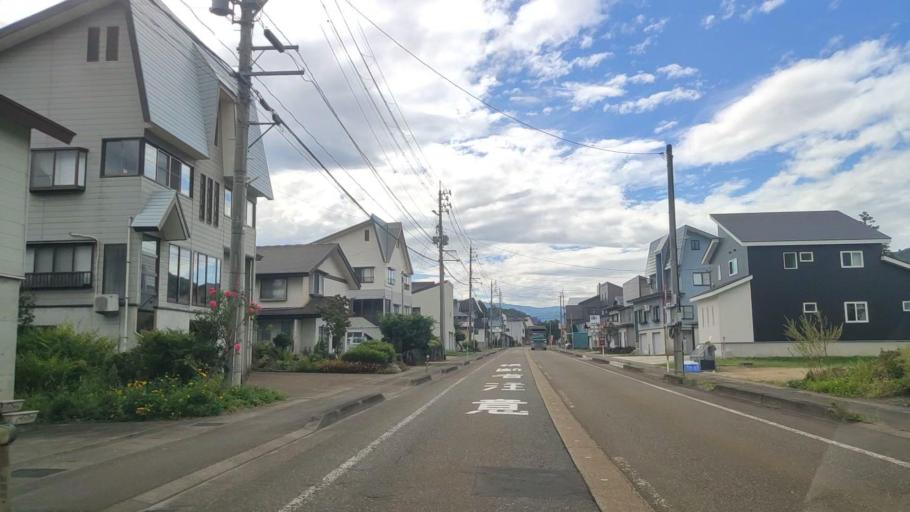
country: JP
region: Niigata
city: Arai
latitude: 36.9845
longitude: 138.2722
